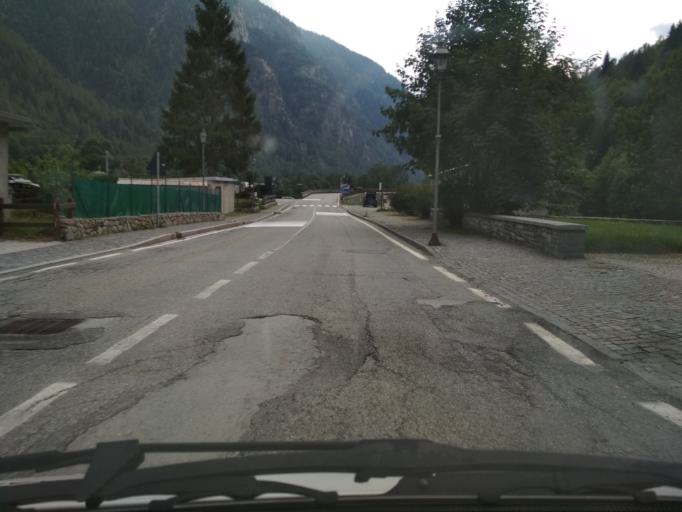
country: IT
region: Aosta Valley
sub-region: Valle d'Aosta
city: Gaby
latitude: 45.7104
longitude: 7.8814
